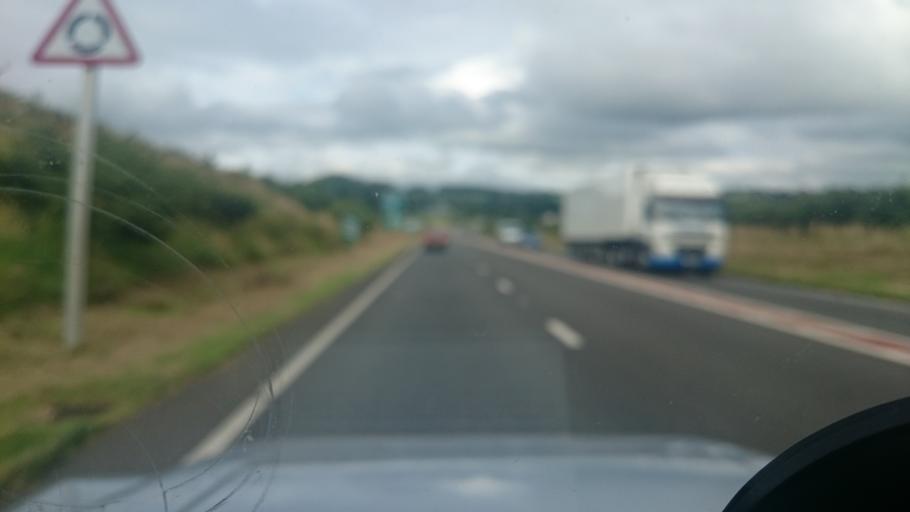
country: GB
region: Wales
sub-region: Pembrokeshire
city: Narberth
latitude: 51.8061
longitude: -4.7777
